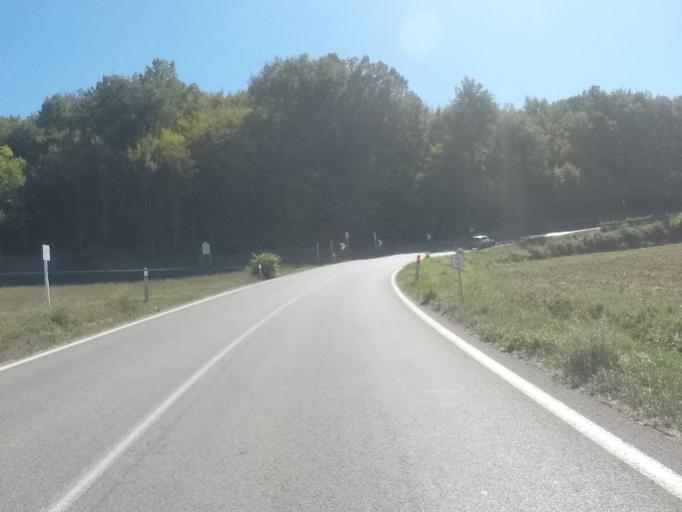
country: IT
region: Tuscany
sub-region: Province of Florence
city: Incisa in Val d'Arno
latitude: 43.6809
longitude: 11.4645
